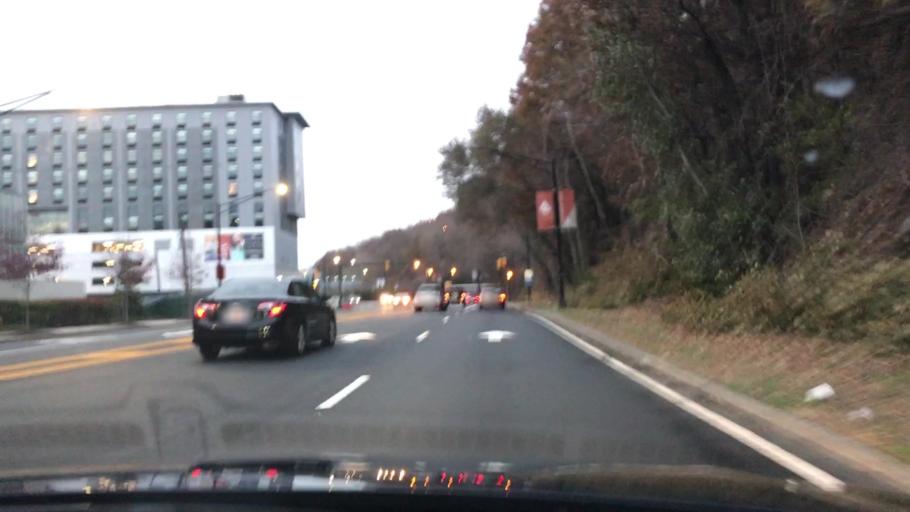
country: US
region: New Jersey
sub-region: Hudson County
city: West New York
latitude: 40.7790
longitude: -74.0111
